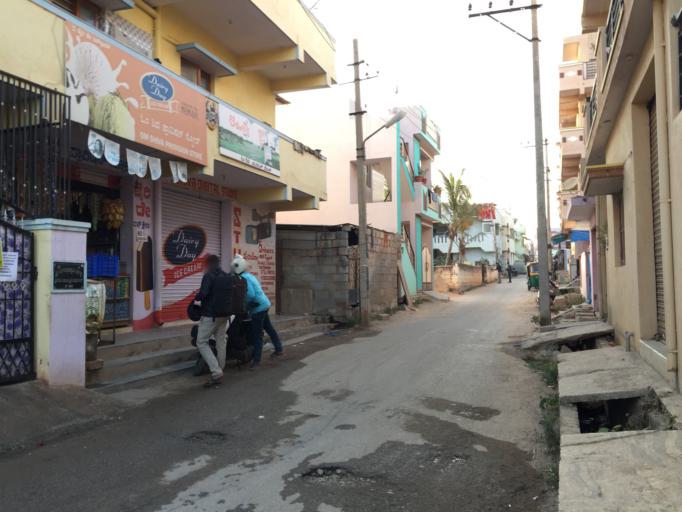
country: IN
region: Karnataka
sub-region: Bangalore Urban
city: Yelahanka
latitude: 13.0524
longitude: 77.6291
